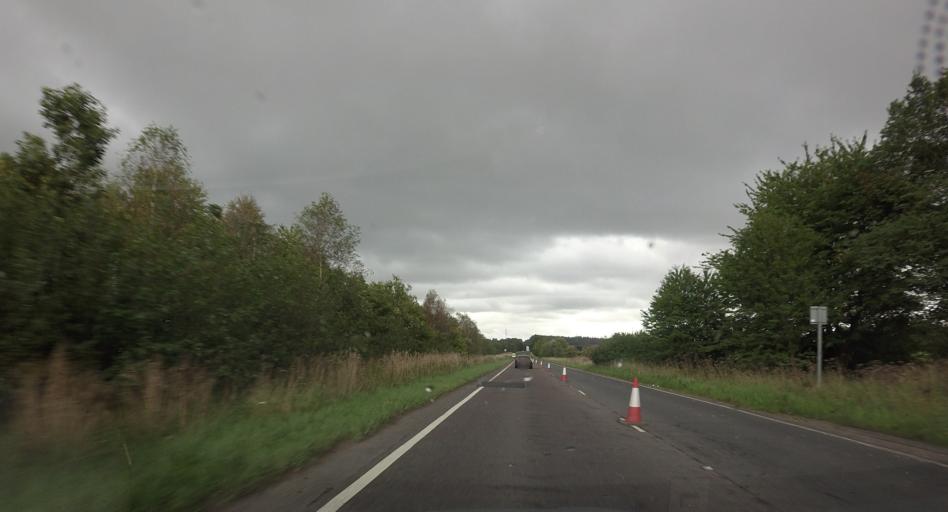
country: GB
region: Scotland
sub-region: Clackmannanshire
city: Clackmannan
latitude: 56.1032
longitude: -3.7286
